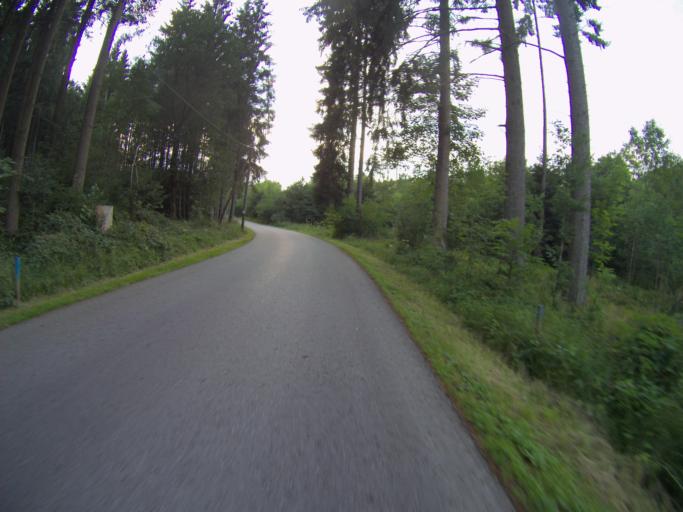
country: DE
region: Bavaria
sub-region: Upper Bavaria
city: Freising
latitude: 48.4204
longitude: 11.7150
